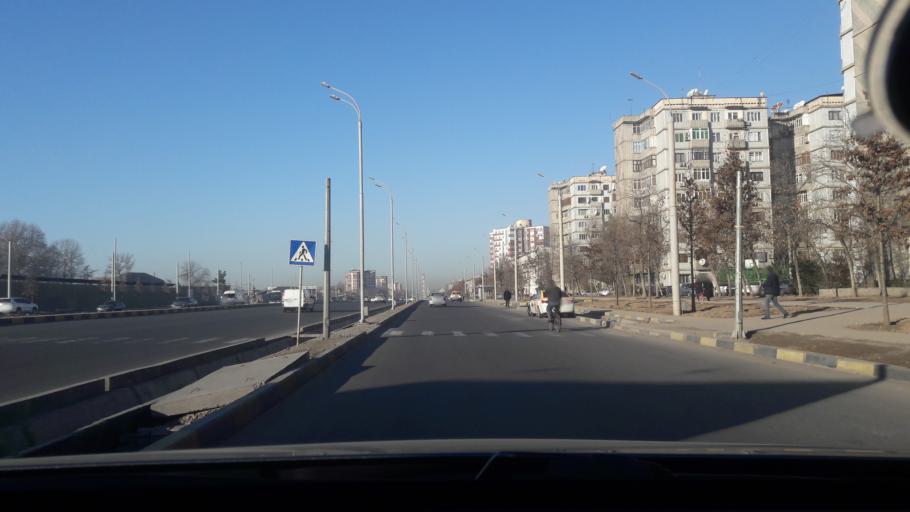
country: TJ
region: Dushanbe
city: Dushanbe
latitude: 38.5586
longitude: 68.7605
